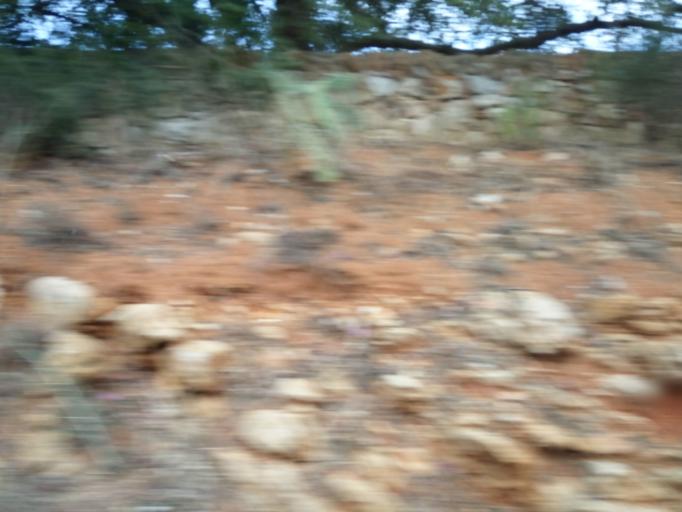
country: PT
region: Faro
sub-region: Faro
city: Santa Barbara de Nexe
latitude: 37.0948
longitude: -7.9631
